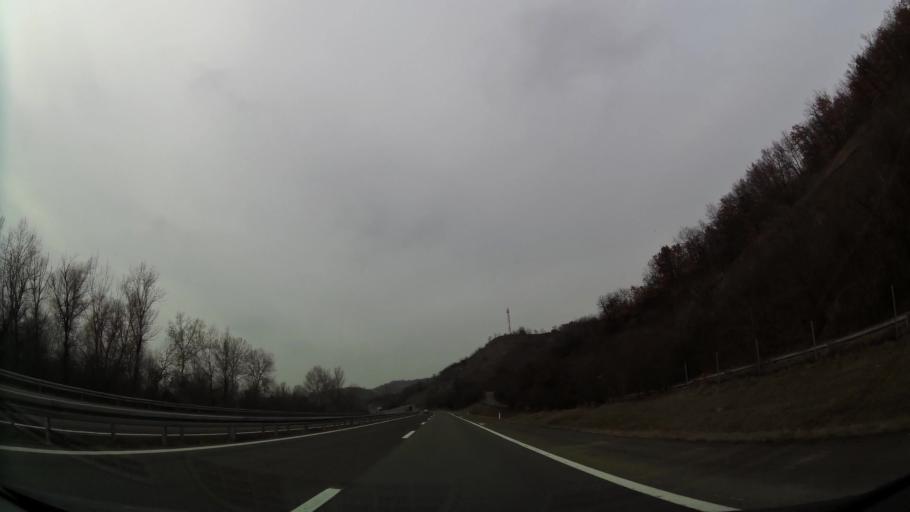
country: RS
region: Central Serbia
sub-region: Nisavski Okrug
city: Aleksinac
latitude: 43.5059
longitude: 21.7526
